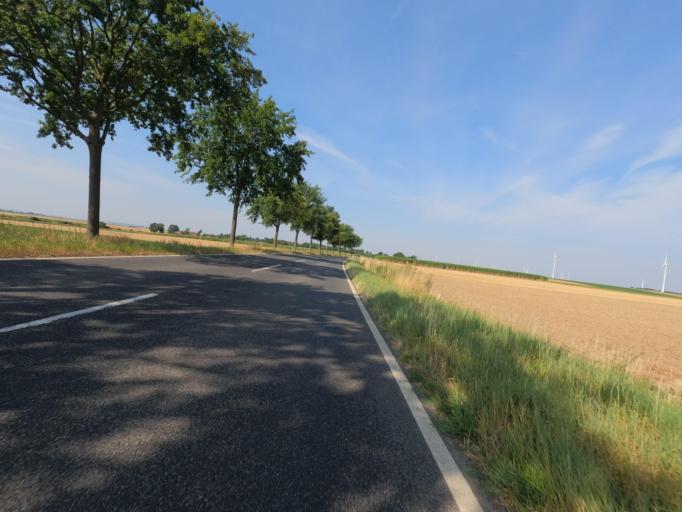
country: DE
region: North Rhine-Westphalia
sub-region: Regierungsbezirk Koln
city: Titz
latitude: 51.0032
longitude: 6.3618
